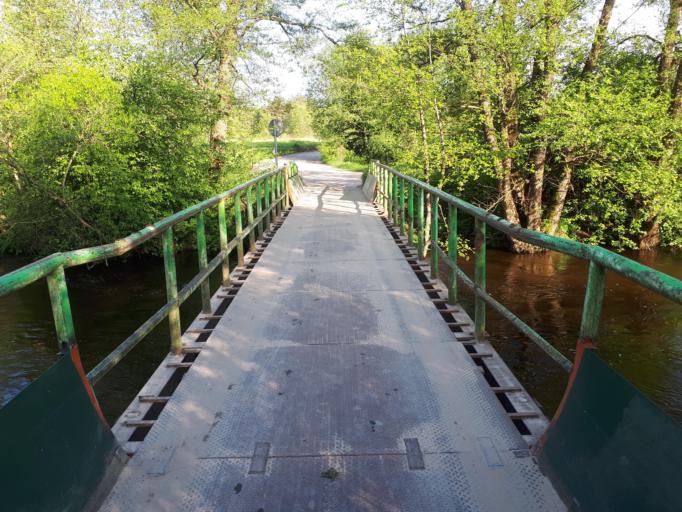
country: LT
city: Skaidiskes
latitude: 54.6875
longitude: 25.4814
